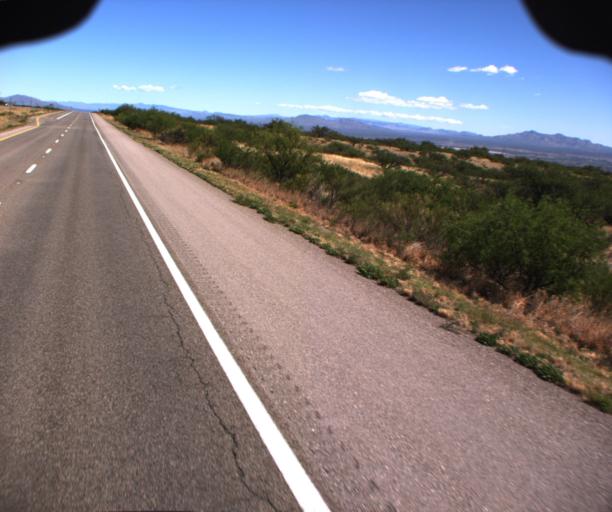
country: US
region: Arizona
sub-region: Cochise County
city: Whetstone
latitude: 31.8789
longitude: -110.3410
